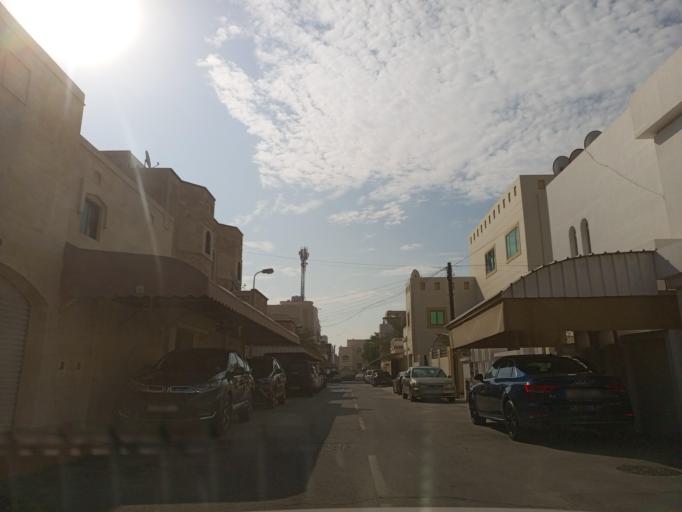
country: BH
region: Muharraq
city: Al Hadd
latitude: 26.2528
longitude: 50.6438
